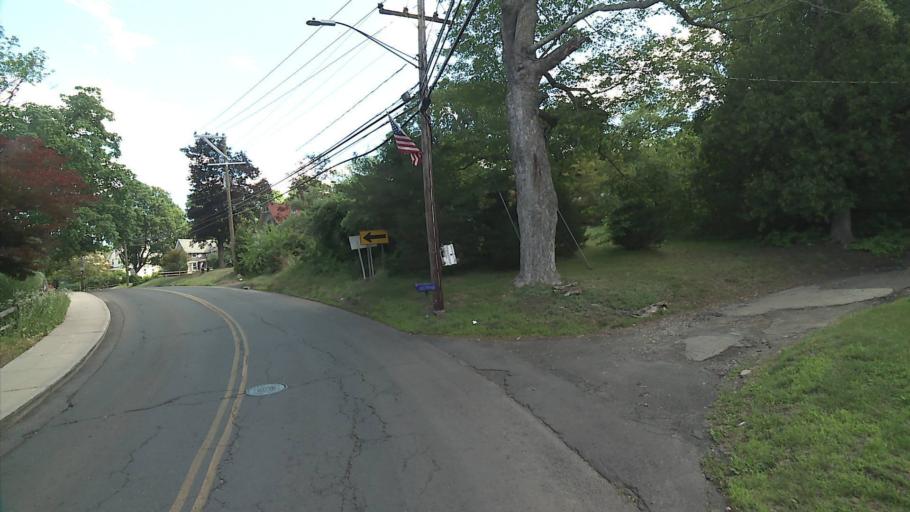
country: US
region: Connecticut
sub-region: Middlesex County
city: East Hampton
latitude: 41.5779
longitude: -72.4987
